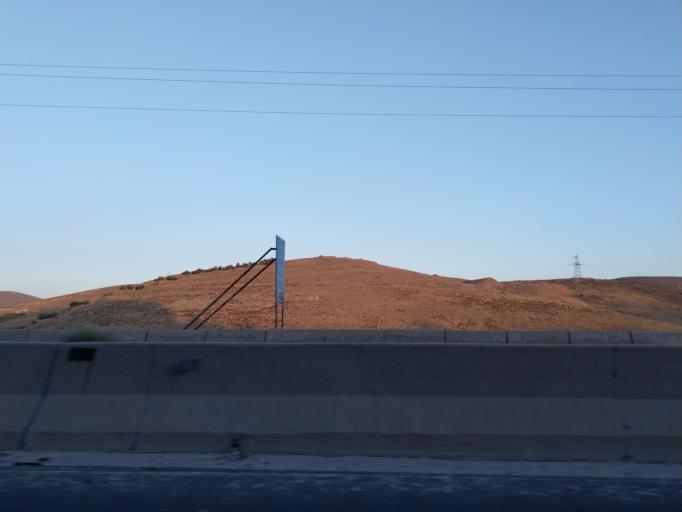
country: SY
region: Rif-dimashq
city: At Tall
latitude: 33.5878
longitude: 36.3078
